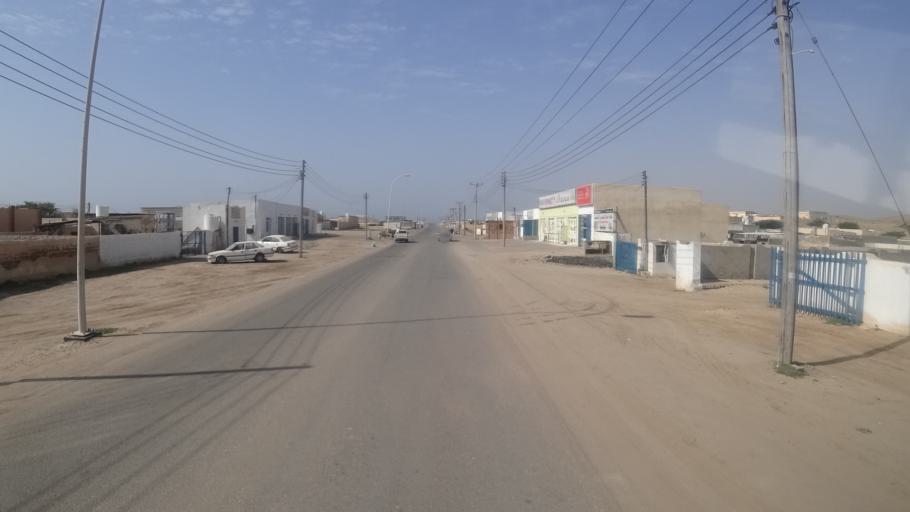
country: OM
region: Ash Sharqiyah
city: Sur
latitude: 22.1777
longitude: 59.7616
